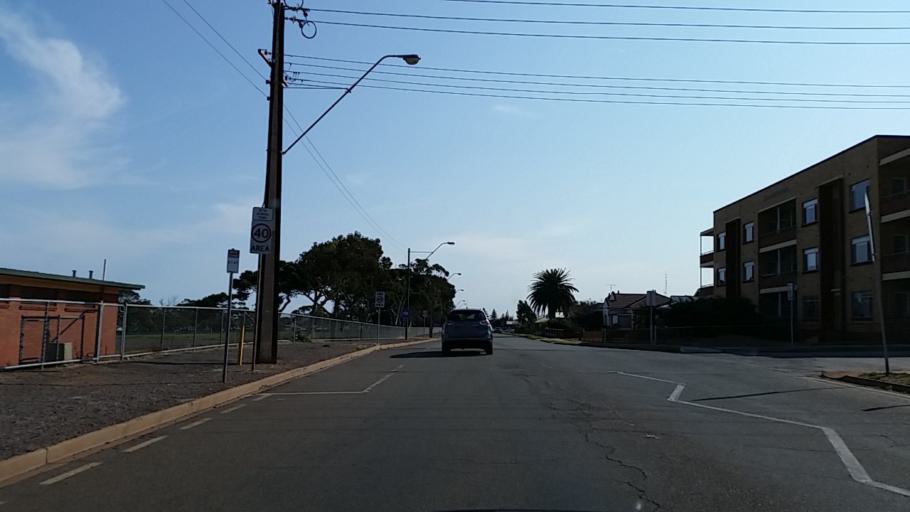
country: AU
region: South Australia
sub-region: Whyalla
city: Whyalla
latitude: -33.0397
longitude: 137.5809
